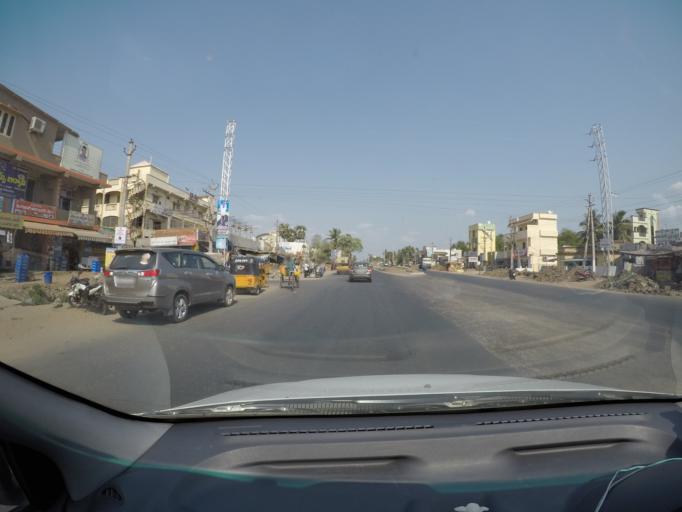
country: IN
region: Andhra Pradesh
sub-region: Krishna
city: Yanamalakuduru
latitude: 16.4763
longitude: 80.7068
